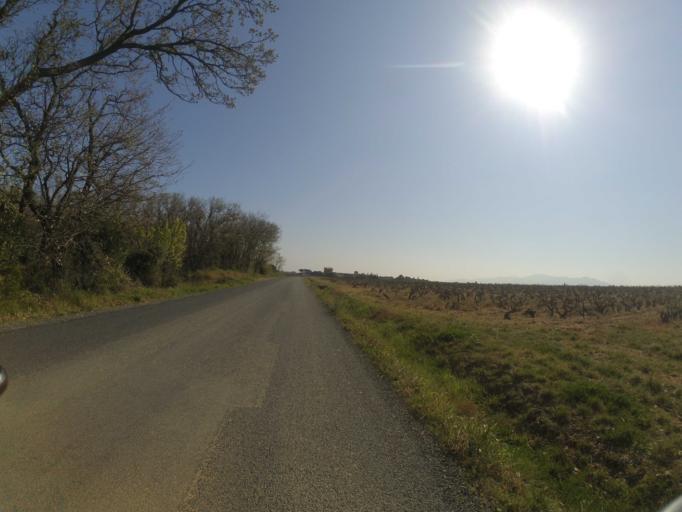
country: FR
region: Languedoc-Roussillon
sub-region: Departement des Pyrenees-Orientales
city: Llupia
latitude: 42.6103
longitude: 2.7625
